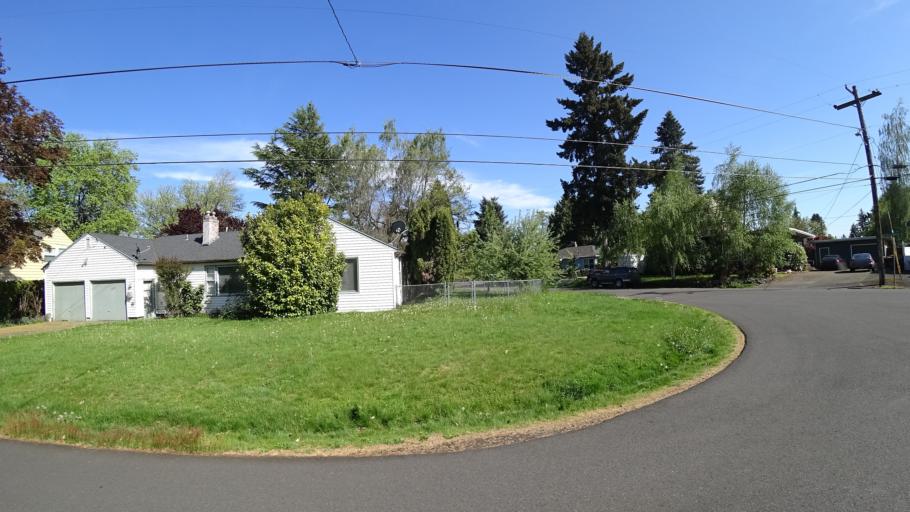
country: US
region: Oregon
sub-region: Washington County
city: Hillsboro
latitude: 45.5263
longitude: -122.9780
